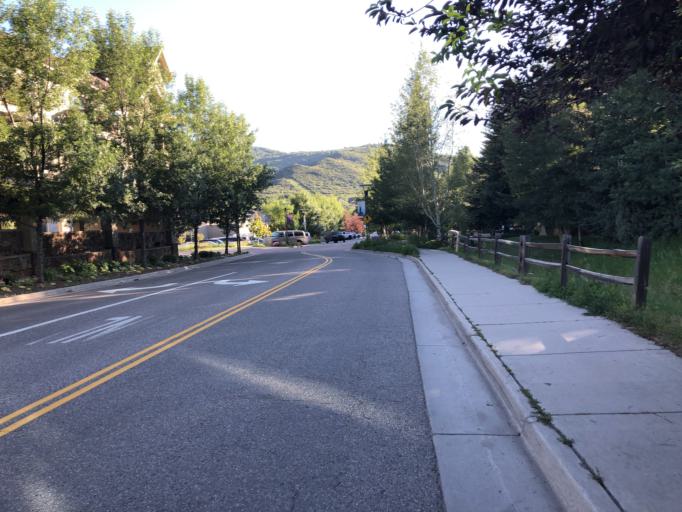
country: US
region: Colorado
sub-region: Eagle County
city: Avon
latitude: 39.6373
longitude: -106.5251
